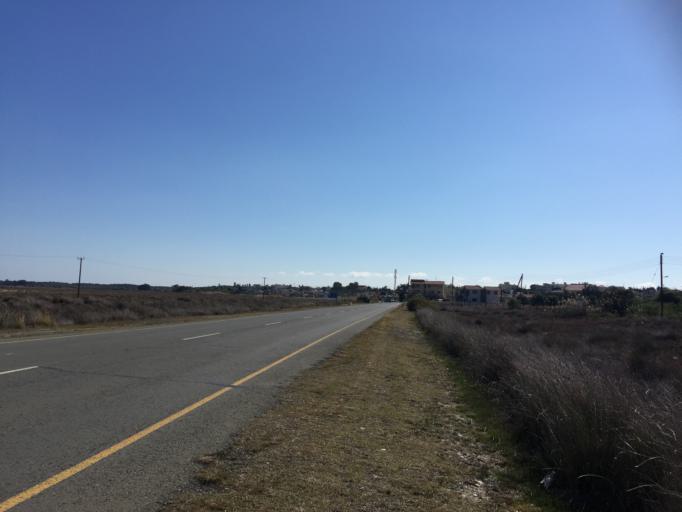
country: CY
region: Larnaka
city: Kolossi
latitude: 34.6080
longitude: 32.9484
